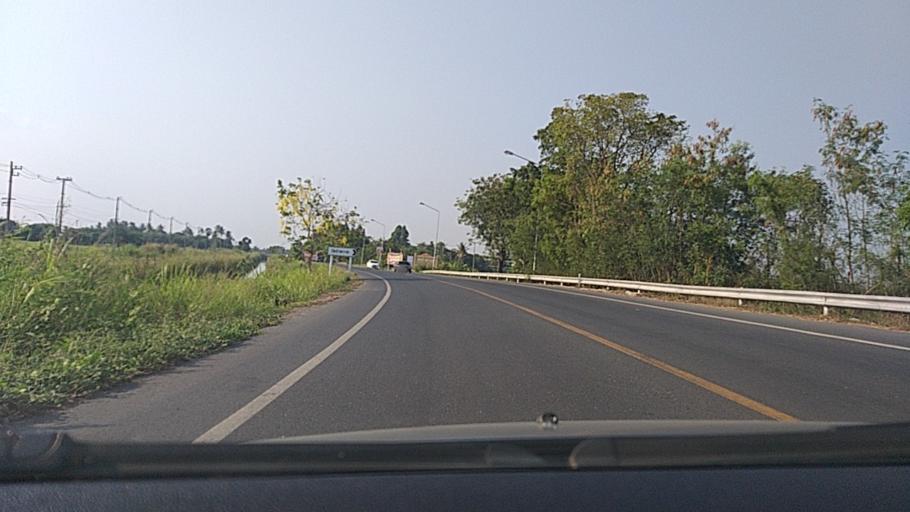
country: TH
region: Sing Buri
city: Phrom Buri
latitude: 14.8139
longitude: 100.4350
